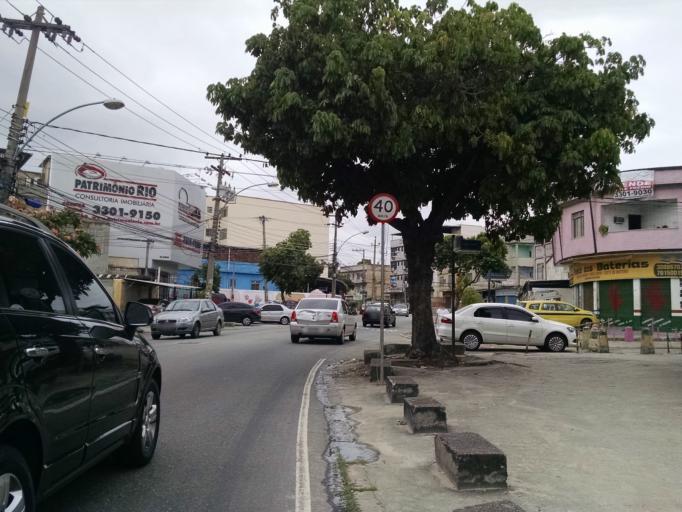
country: BR
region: Rio de Janeiro
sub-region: Duque De Caxias
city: Duque de Caxias
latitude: -22.8379
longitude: -43.3137
